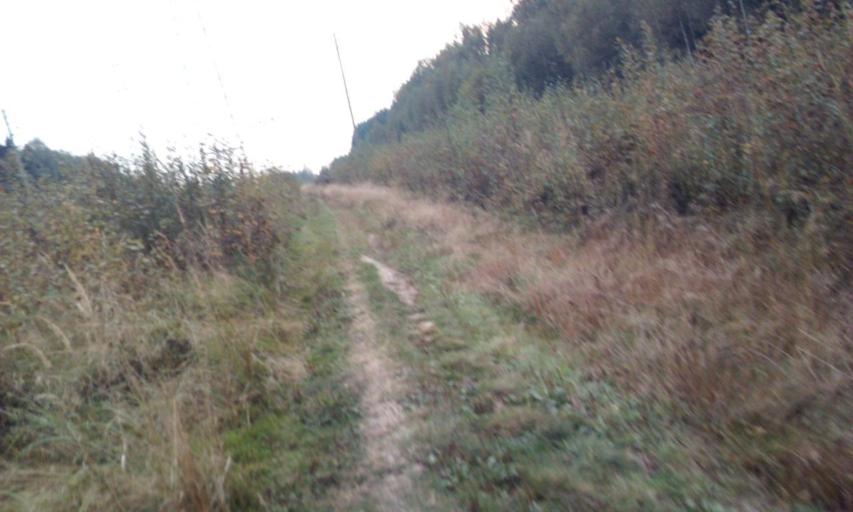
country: RU
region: Moskovskaya
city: Aprelevka
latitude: 55.5710
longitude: 37.0809
